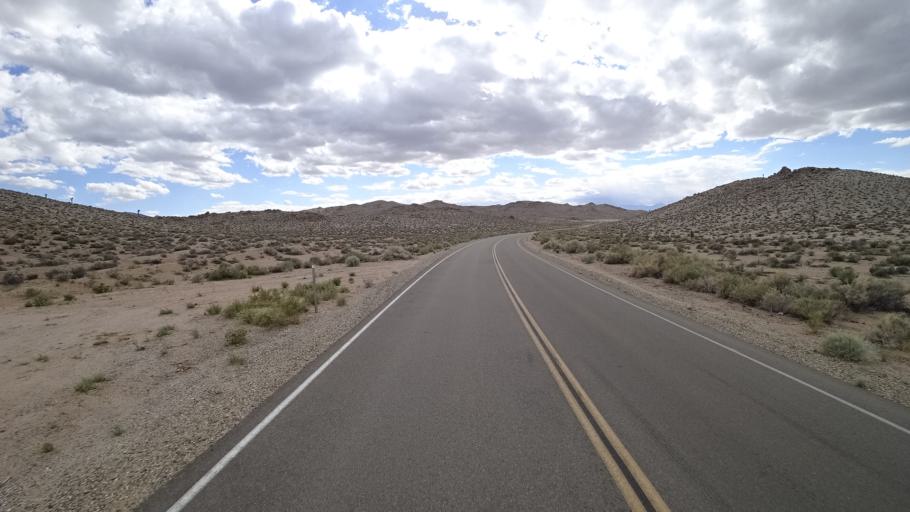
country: US
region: California
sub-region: Inyo County
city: Lone Pine
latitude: 36.3159
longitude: -117.6781
